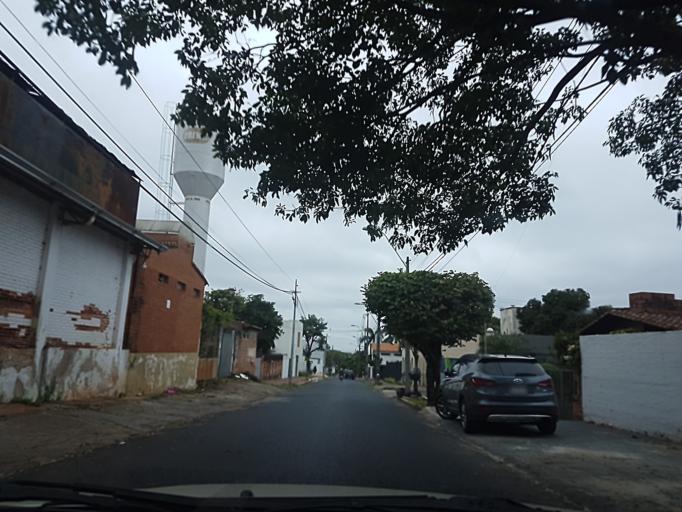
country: PY
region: Asuncion
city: Asuncion
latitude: -25.2986
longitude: -57.6029
